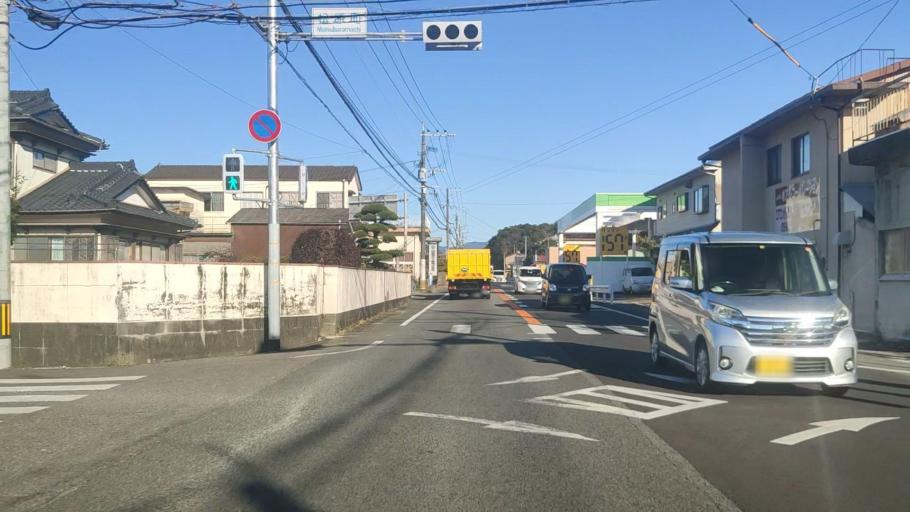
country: JP
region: Miyazaki
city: Nobeoka
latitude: 32.5242
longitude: 131.6830
